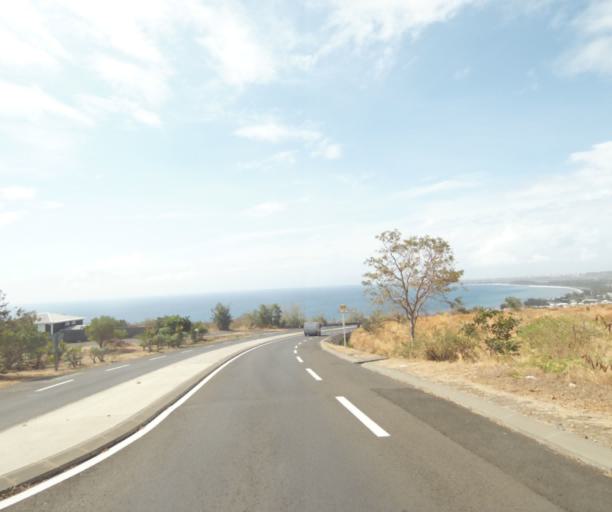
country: RE
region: Reunion
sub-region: Reunion
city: Saint-Paul
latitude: -21.0182
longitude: 55.2655
